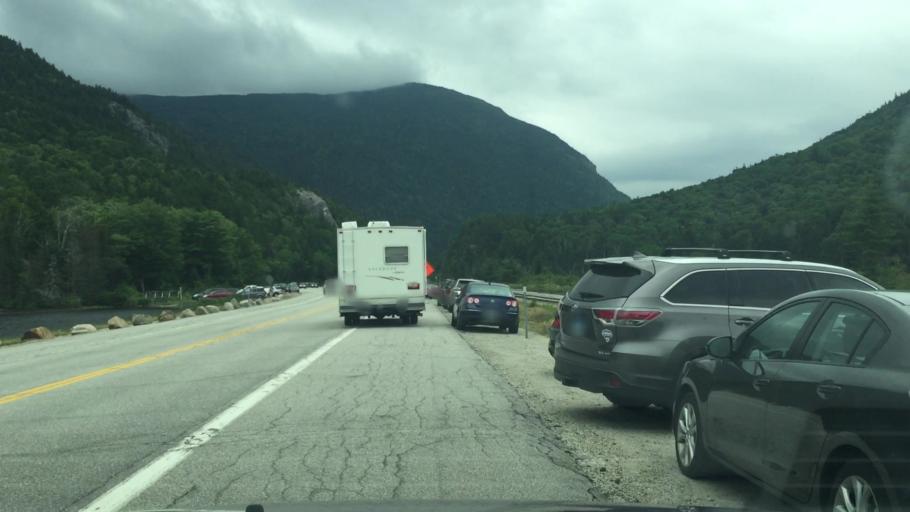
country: US
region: New Hampshire
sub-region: Grafton County
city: Deerfield
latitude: 44.2169
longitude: -71.4103
